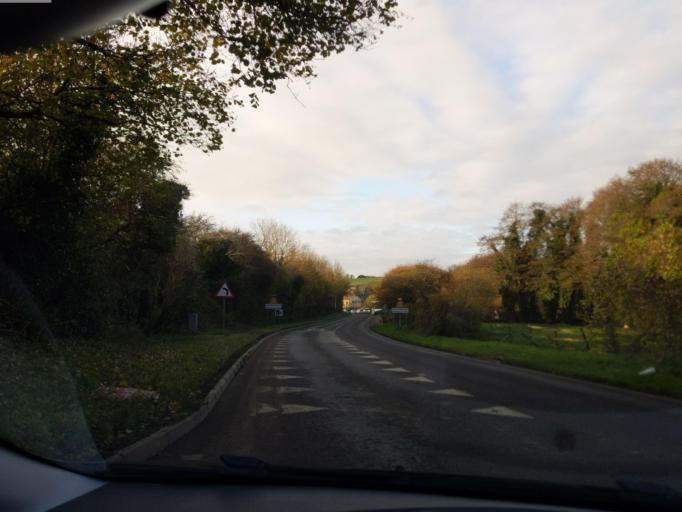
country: GB
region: England
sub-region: Cornwall
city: Wadebridge
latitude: 50.5082
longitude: -4.8031
